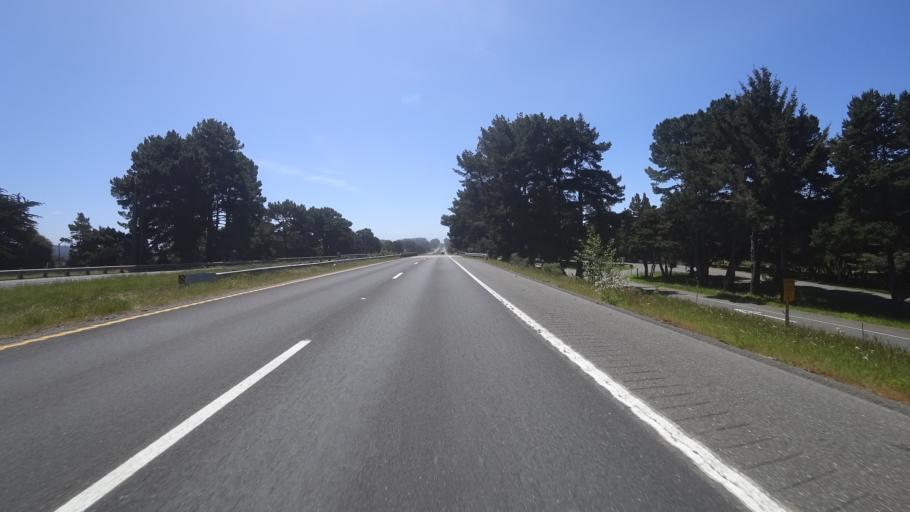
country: US
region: California
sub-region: Humboldt County
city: McKinleyville
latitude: 40.9698
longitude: -124.1162
